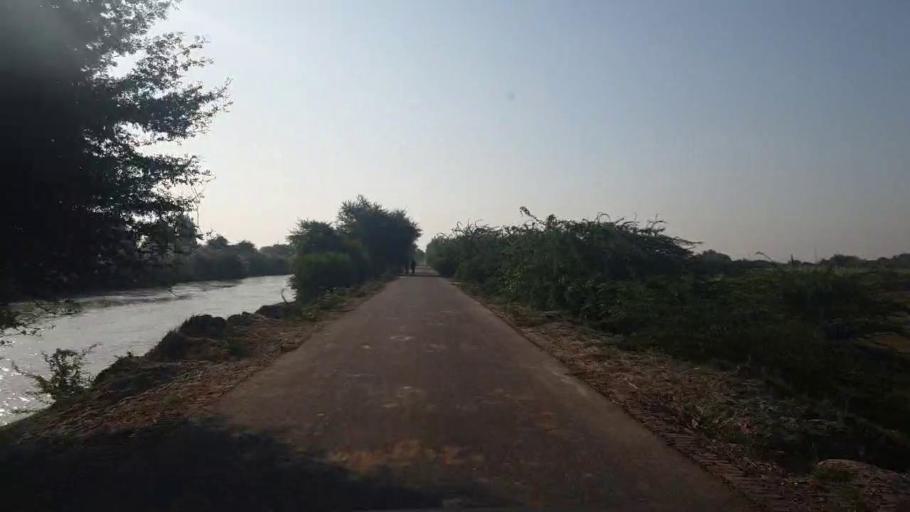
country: PK
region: Sindh
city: Tando Bago
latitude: 24.7291
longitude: 68.9368
